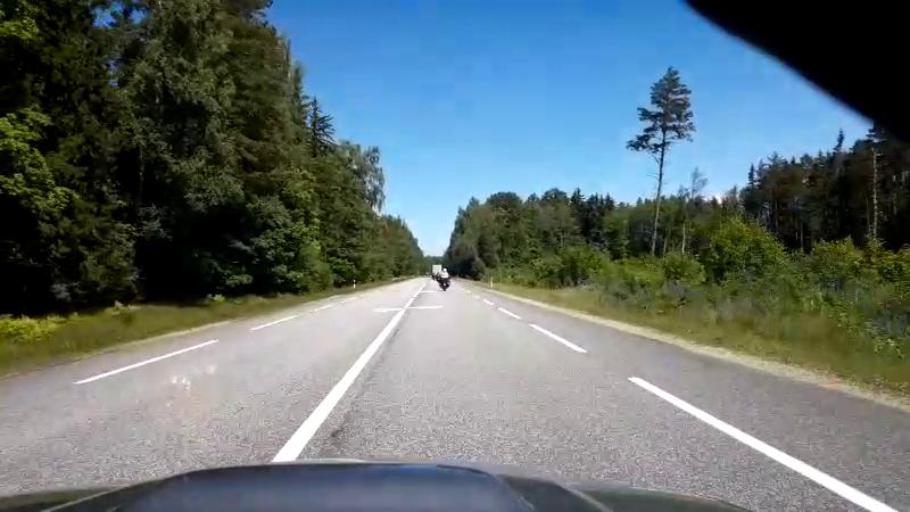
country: LV
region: Saulkrastu
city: Saulkrasti
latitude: 57.3936
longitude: 24.4285
